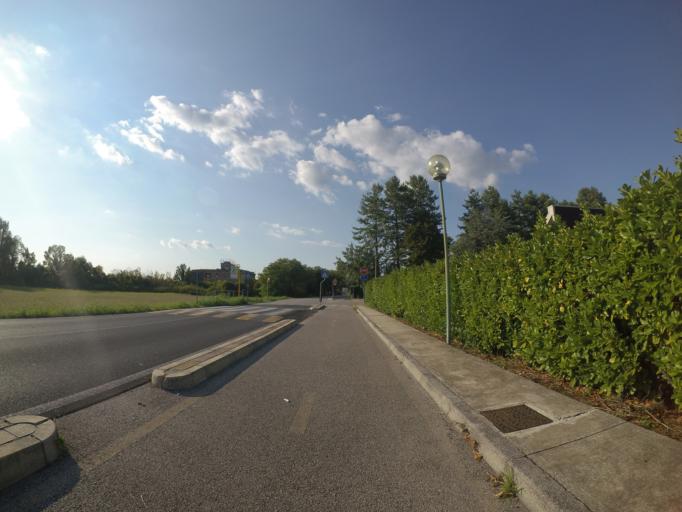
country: IT
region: Friuli Venezia Giulia
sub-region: Provincia di Udine
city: Pasian di Prato
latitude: 46.0424
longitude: 13.1991
